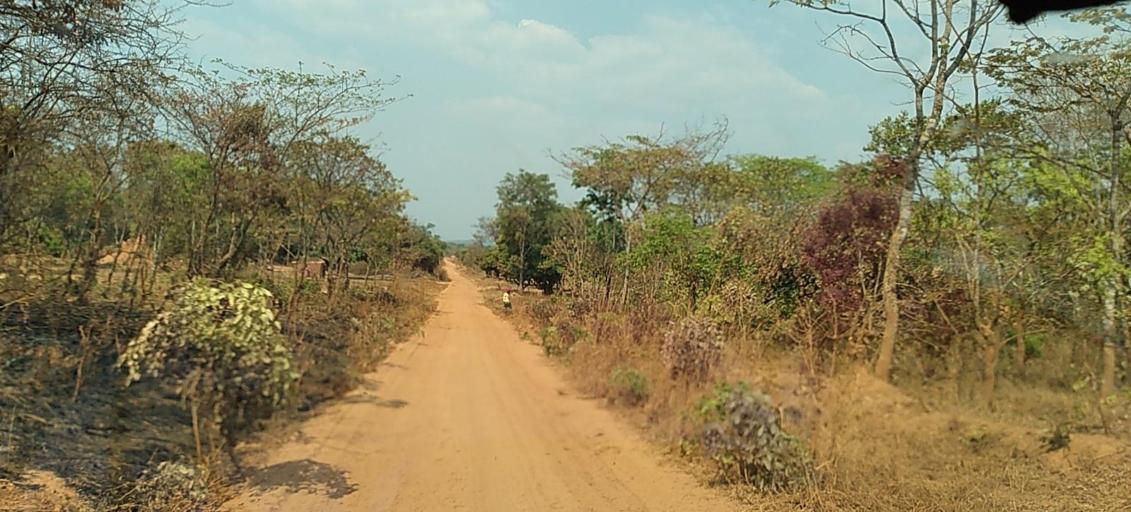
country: ZM
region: North-Western
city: Kasempa
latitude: -13.3061
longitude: 26.0722
